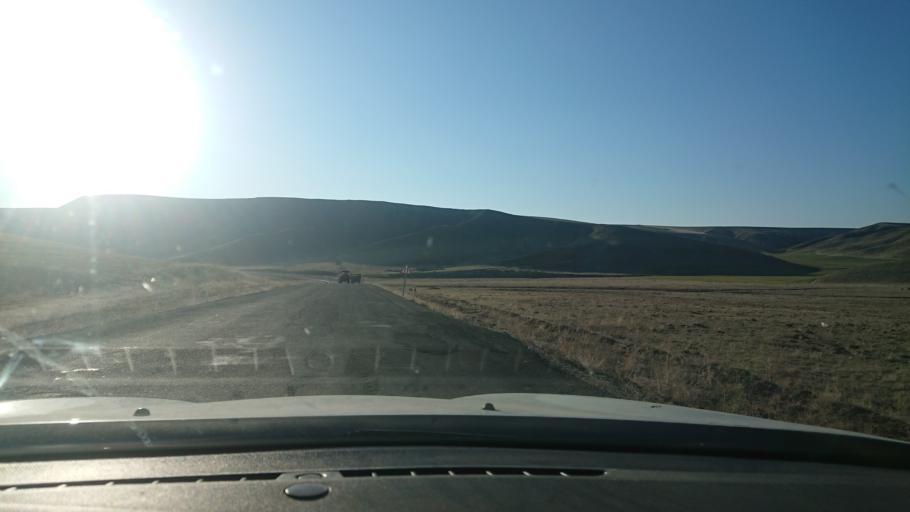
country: TR
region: Aksaray
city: Acipinar
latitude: 38.7115
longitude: 33.7639
